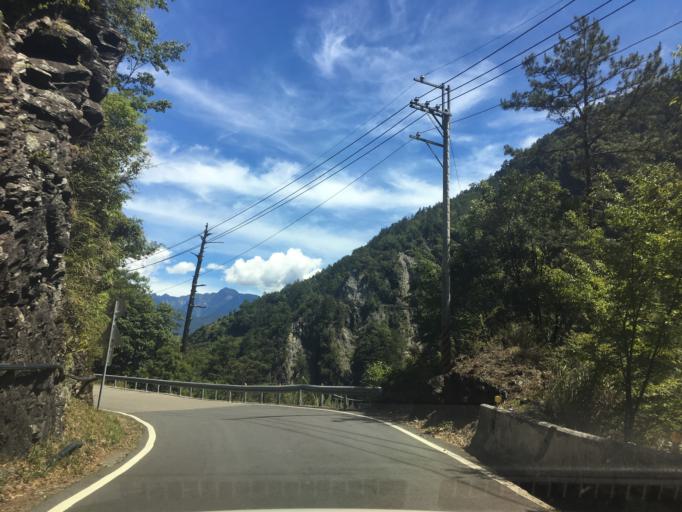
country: TW
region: Taiwan
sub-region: Nantou
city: Puli
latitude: 24.2211
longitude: 121.2638
